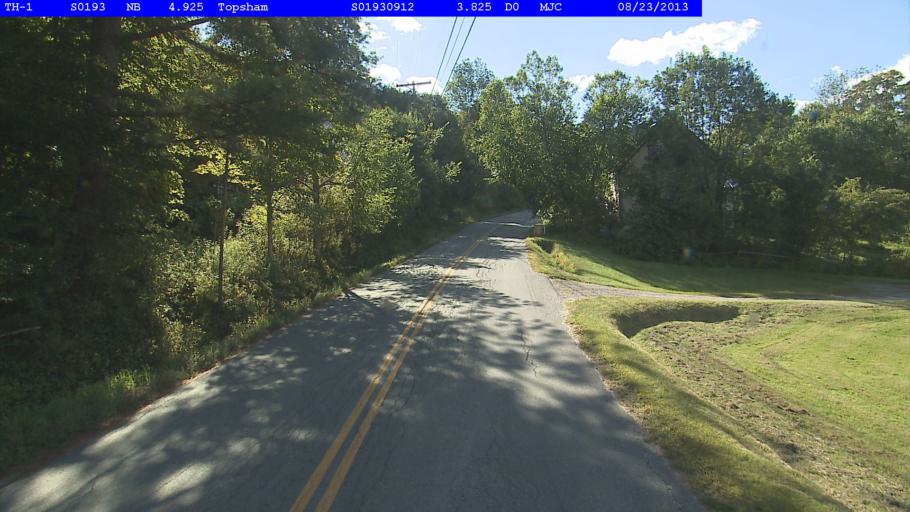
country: US
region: New Hampshire
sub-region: Grafton County
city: Haverhill
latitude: 44.1213
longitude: -72.2346
